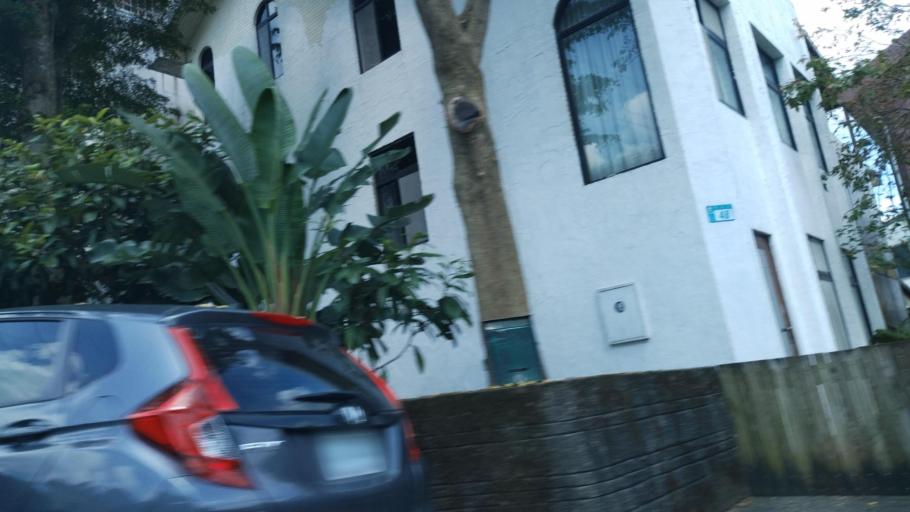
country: TW
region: Taipei
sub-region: Taipei
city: Banqiao
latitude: 24.9505
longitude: 121.4993
